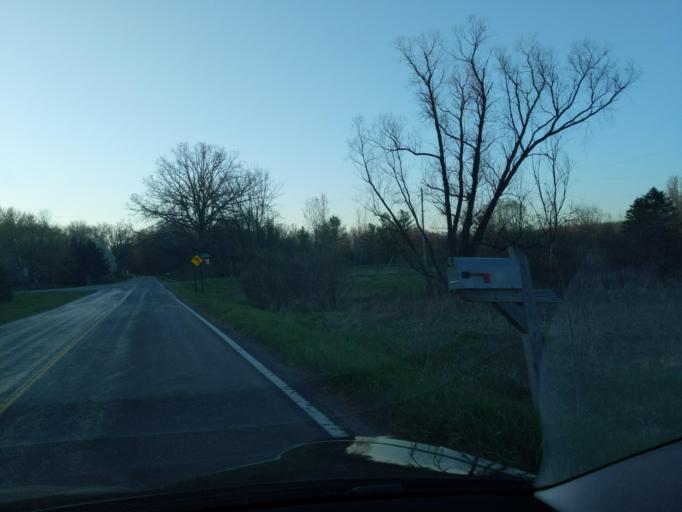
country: US
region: Michigan
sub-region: Ingham County
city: Stockbridge
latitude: 42.4825
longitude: -84.2130
